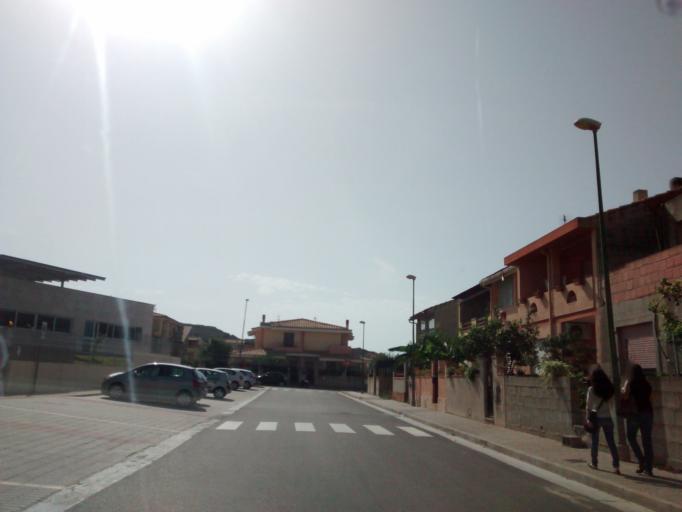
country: IT
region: Sardinia
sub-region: Provincia di Cagliari
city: Villasimius
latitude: 39.1483
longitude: 9.5187
